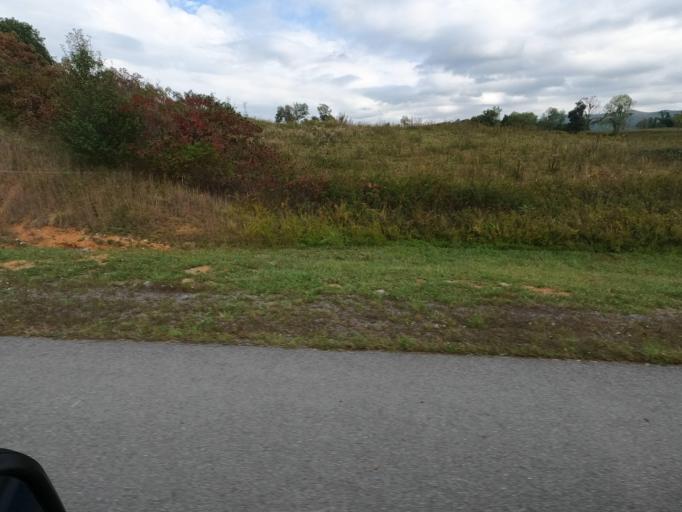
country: US
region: Tennessee
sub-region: Carter County
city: Central
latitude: 36.3030
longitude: -82.2467
